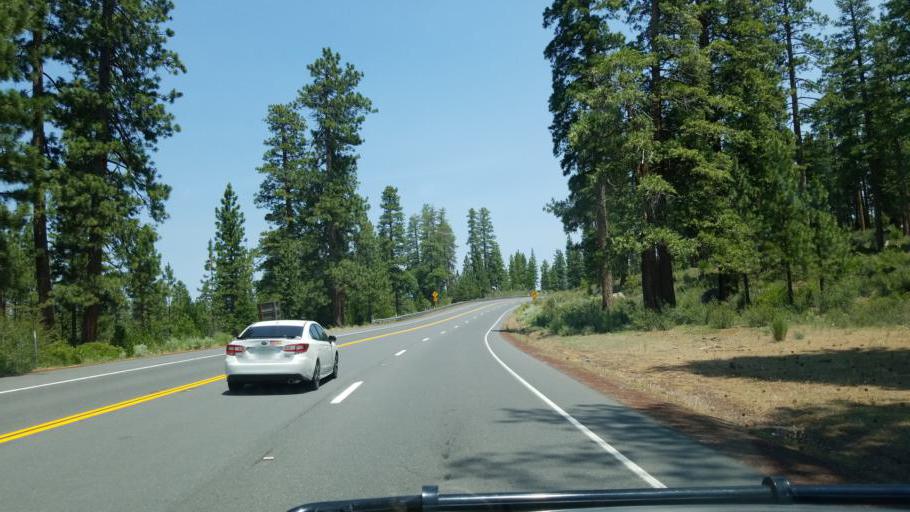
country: US
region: California
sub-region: Shasta County
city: Burney
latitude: 40.7008
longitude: -121.4002
